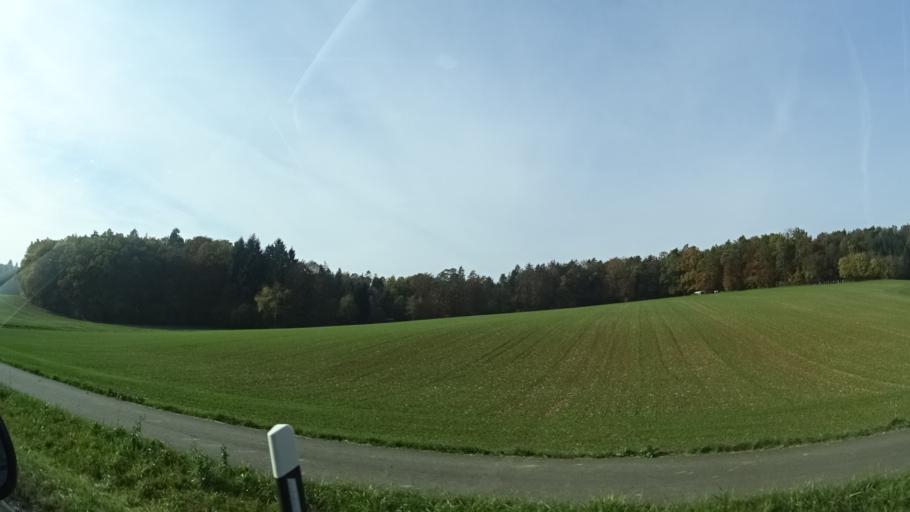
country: DE
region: Baden-Wuerttemberg
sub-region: Regierungsbezirk Stuttgart
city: Igersheim
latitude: 49.5265
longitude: 9.8419
